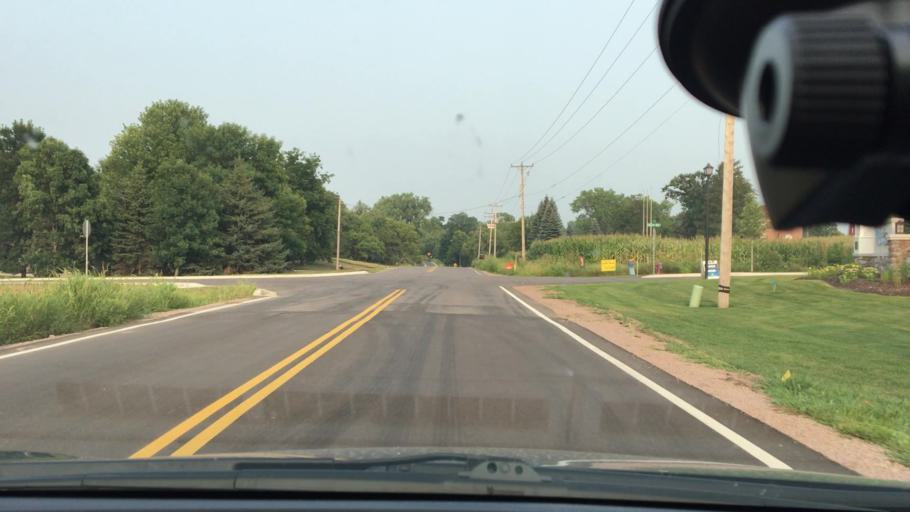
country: US
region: Minnesota
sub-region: Wright County
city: Saint Michael
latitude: 45.2101
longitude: -93.6298
